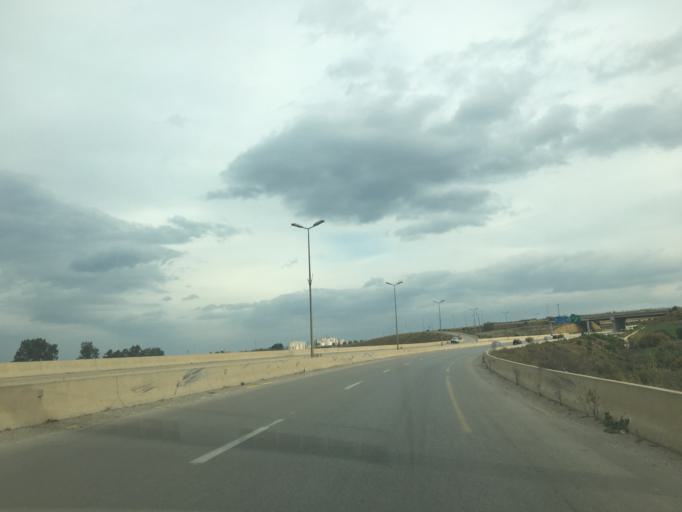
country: DZ
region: Tipaza
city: Tipasa
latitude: 36.5760
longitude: 2.4214
